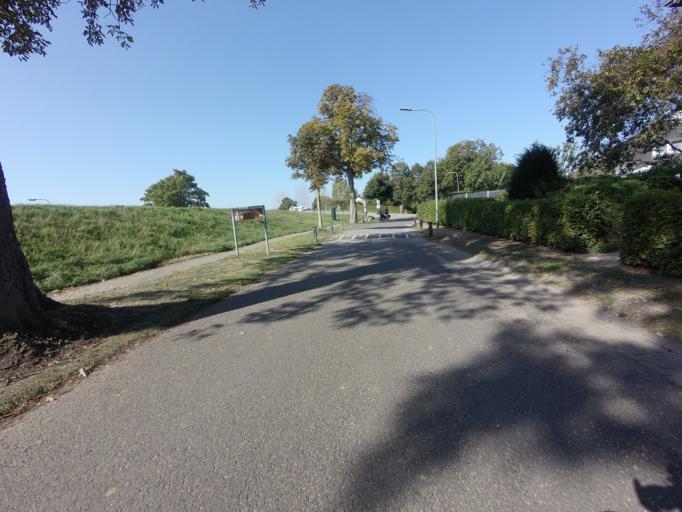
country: NL
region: Limburg
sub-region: Gemeente Roermond
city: Roermond
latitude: 51.1876
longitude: 5.9473
